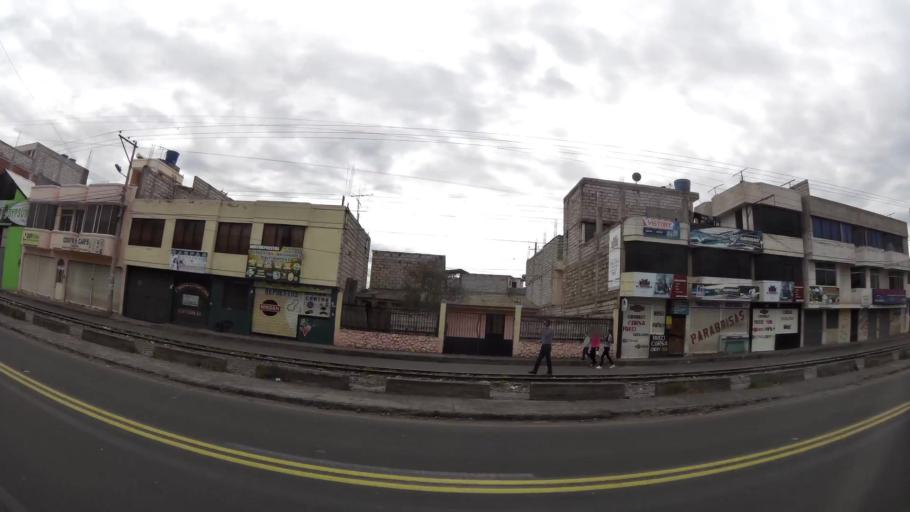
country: EC
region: Cotopaxi
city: Latacunga
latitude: -0.9292
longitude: -78.6241
